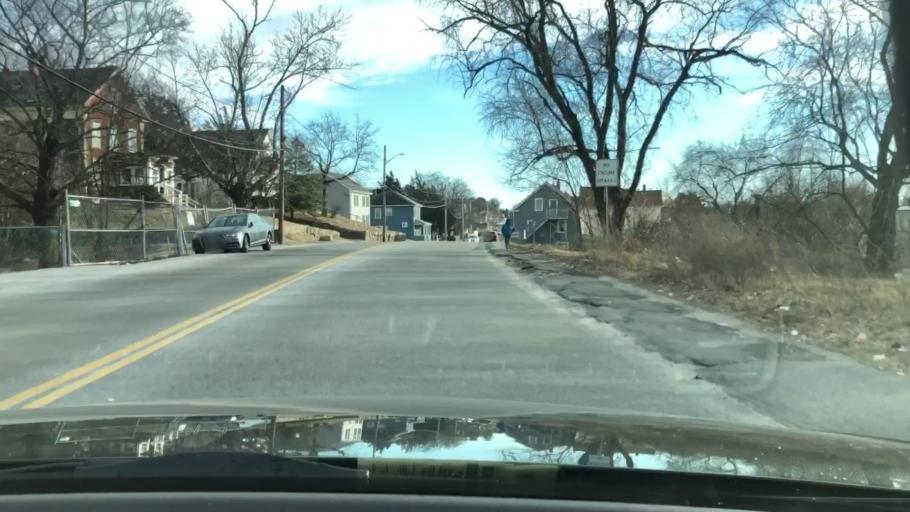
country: US
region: Massachusetts
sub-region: Worcester County
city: Milford
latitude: 42.1423
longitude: -71.5126
